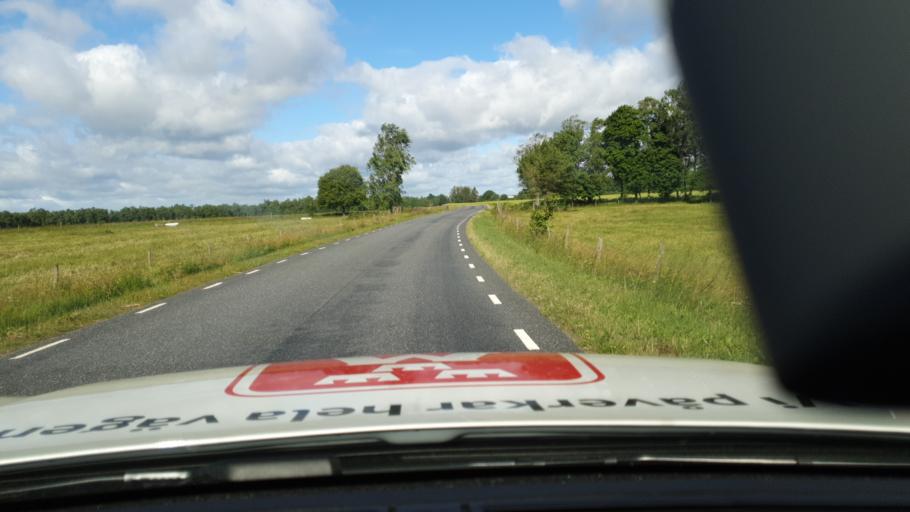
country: SE
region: Vaestra Goetaland
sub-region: Falkopings Kommun
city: Floby
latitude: 58.1256
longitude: 13.3821
